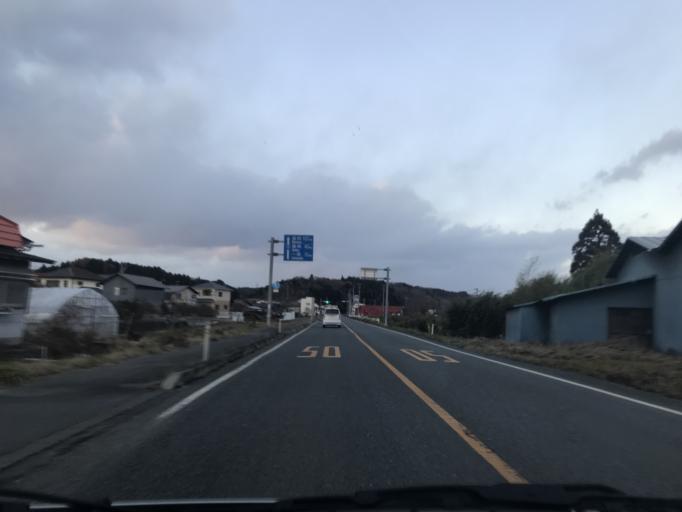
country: JP
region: Iwate
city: Ichinoseki
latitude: 38.8134
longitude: 141.0773
